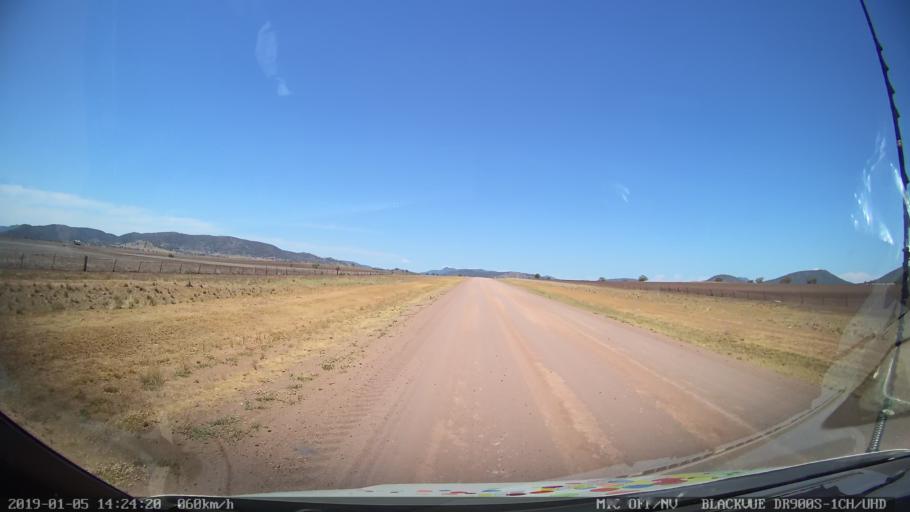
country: AU
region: New South Wales
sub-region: Liverpool Plains
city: Quirindi
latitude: -31.2418
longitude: 150.5388
